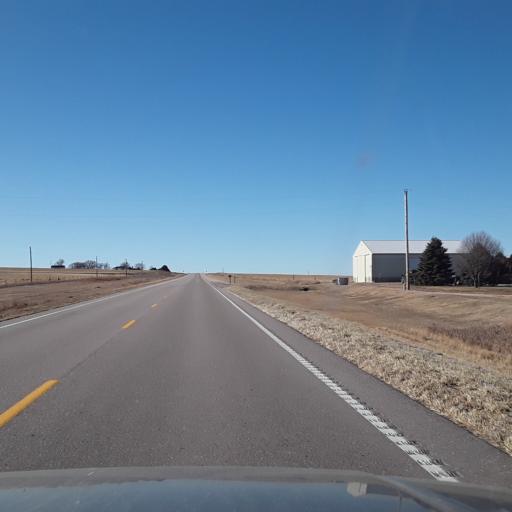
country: US
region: Nebraska
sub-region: Frontier County
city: Stockville
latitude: 40.7003
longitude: -100.2702
